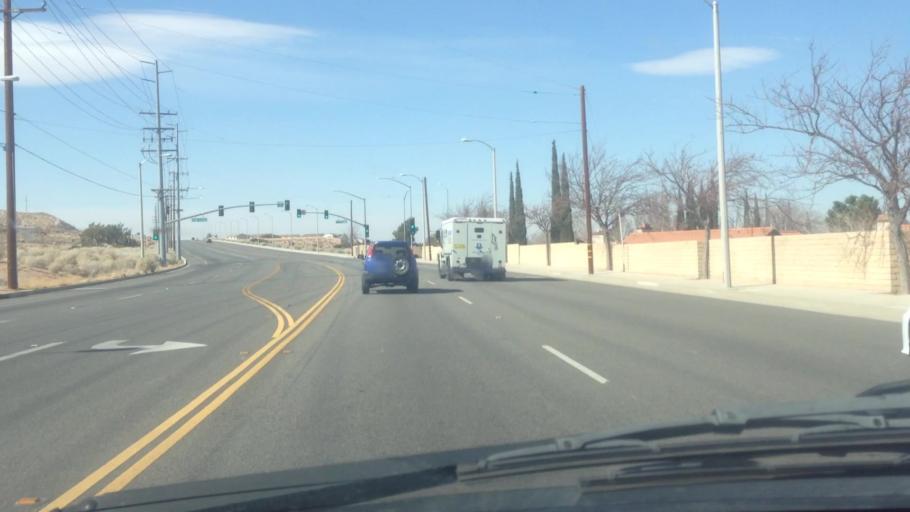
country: US
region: California
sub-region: Los Angeles County
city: Desert View Highlands
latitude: 34.5713
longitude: -118.1397
